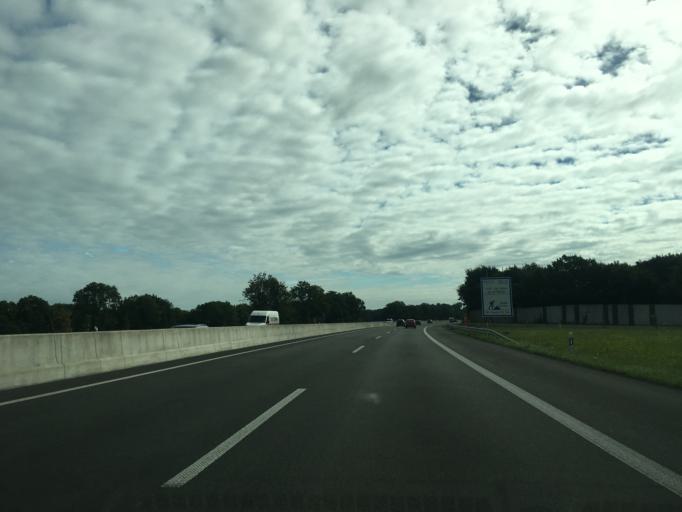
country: DE
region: North Rhine-Westphalia
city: Loehne
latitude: 52.2081
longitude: 8.7092
